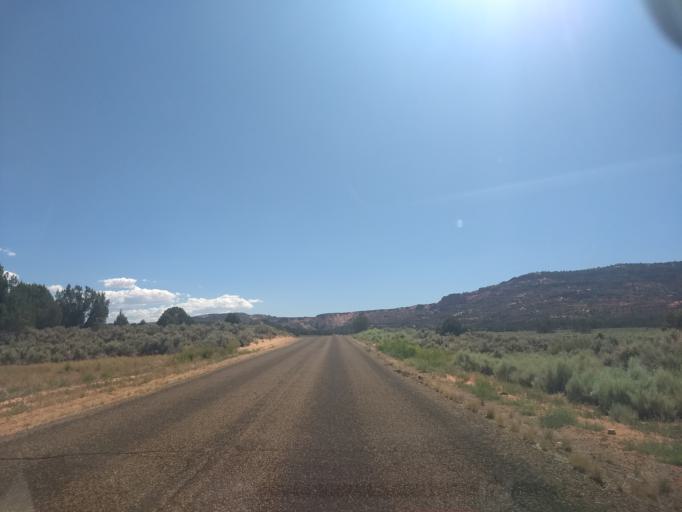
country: US
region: Utah
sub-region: Washington County
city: Hildale
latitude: 37.0135
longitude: -112.8434
